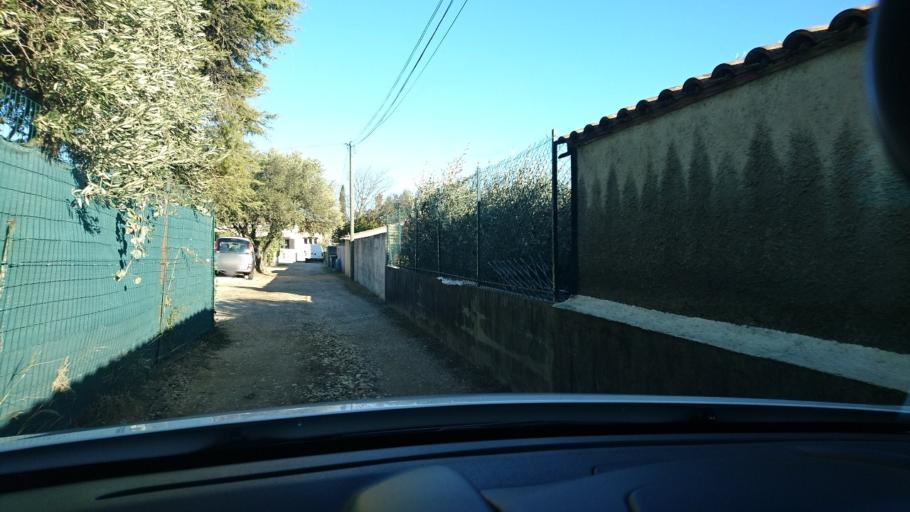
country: FR
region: Languedoc-Roussillon
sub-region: Departement du Gard
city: Les Angles
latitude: 43.9625
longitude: 4.7598
